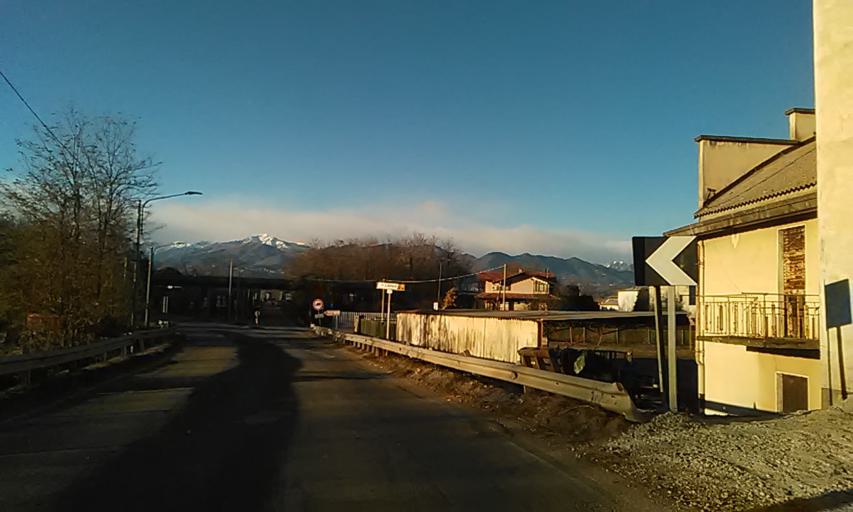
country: IT
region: Piedmont
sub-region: Provincia di Biella
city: Cossato
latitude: 45.5422
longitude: 8.1822
